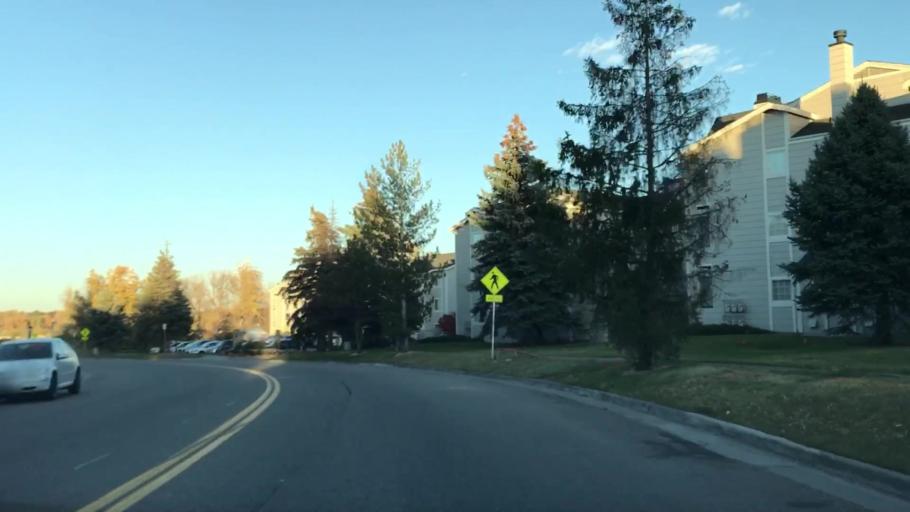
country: US
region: Colorado
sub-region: Arapahoe County
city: Glendale
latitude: 39.6676
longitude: -104.8933
